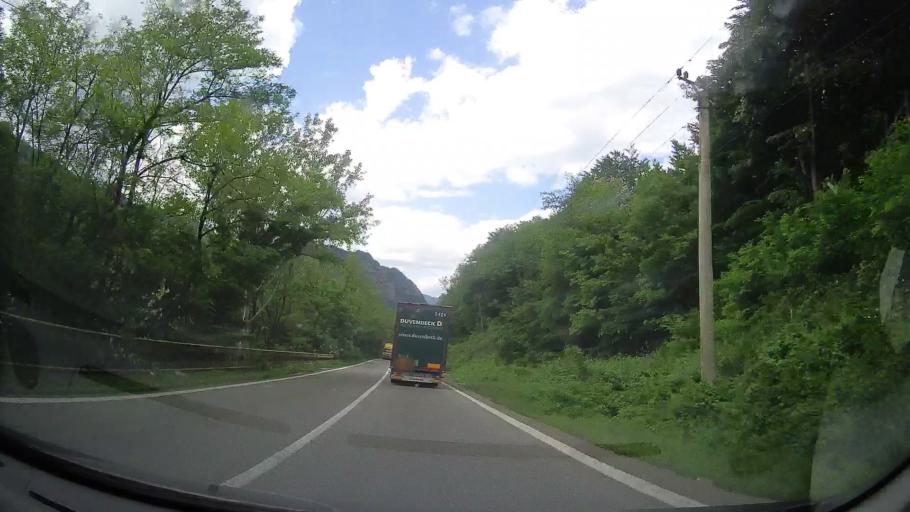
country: RO
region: Valcea
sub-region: Oras Calimanesti
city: Calimanesti
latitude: 45.2693
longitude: 24.3217
